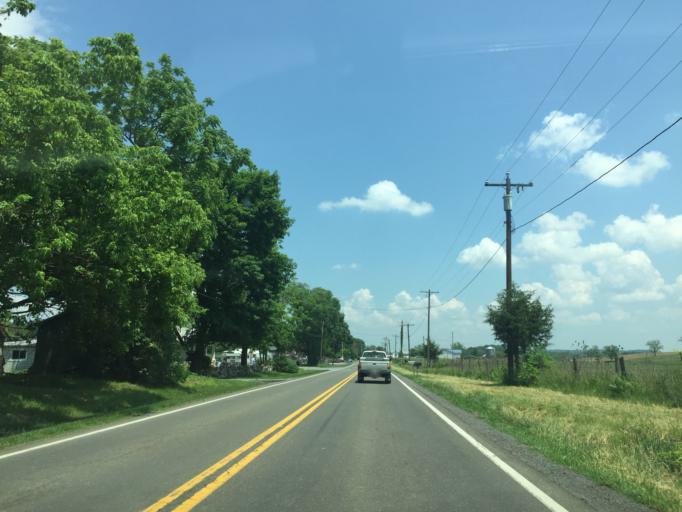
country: US
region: Virginia
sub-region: Shenandoah County
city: Strasburg
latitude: 39.0507
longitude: -78.3719
